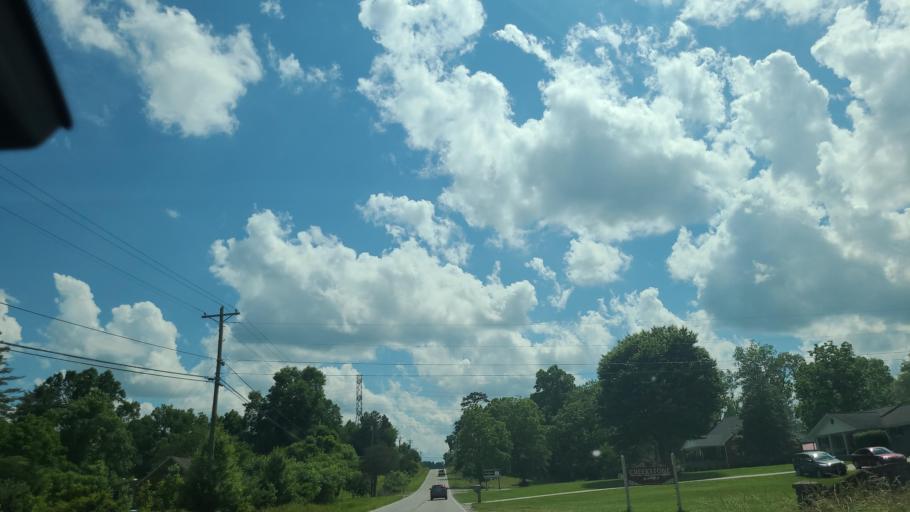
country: US
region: Kentucky
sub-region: Whitley County
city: Corbin
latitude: 36.8881
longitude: -84.1916
